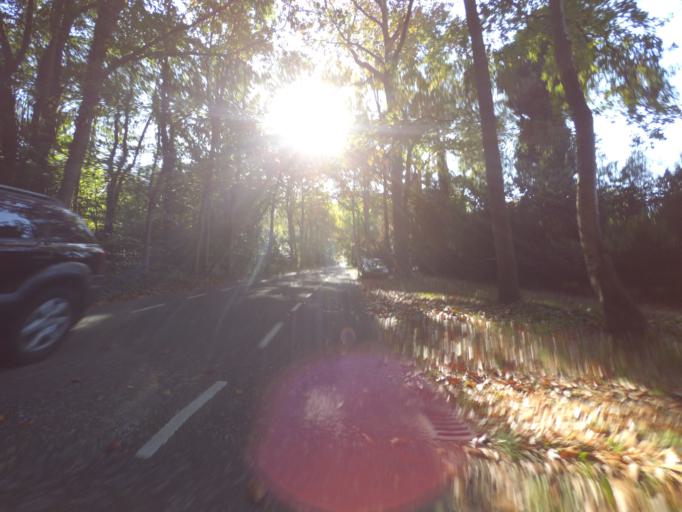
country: NL
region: Utrecht
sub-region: Gemeente Soest
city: Soest
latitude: 52.1201
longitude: 5.2922
